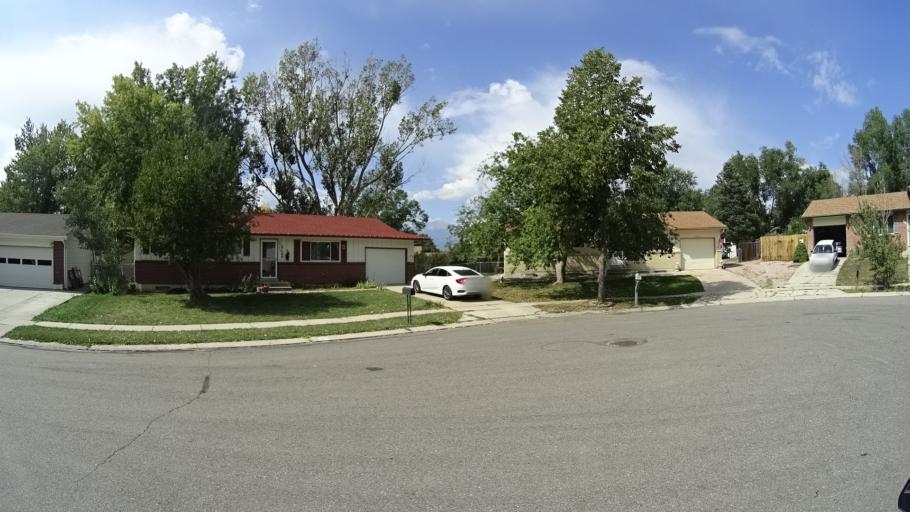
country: US
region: Colorado
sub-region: El Paso County
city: Cimarron Hills
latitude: 38.8535
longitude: -104.7422
